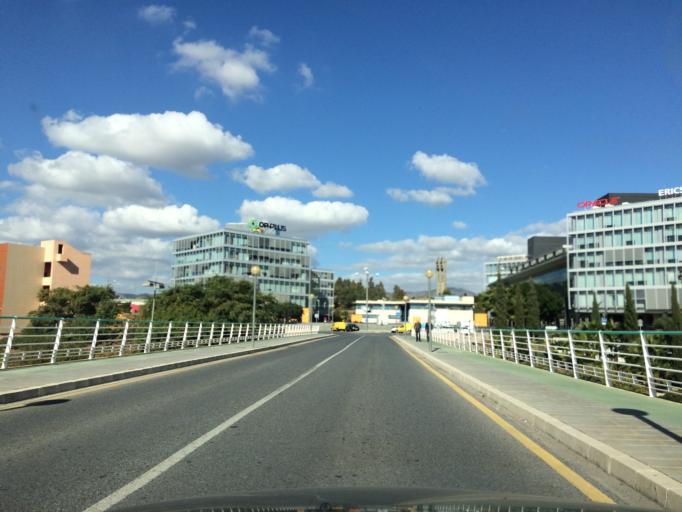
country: ES
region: Andalusia
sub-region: Provincia de Malaga
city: Estacion de Cartama
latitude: 36.7376
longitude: -4.5536
